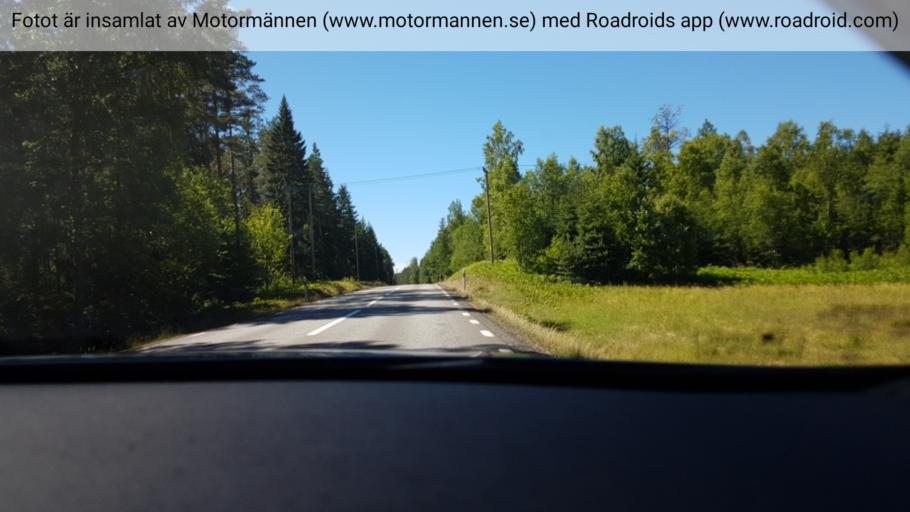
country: SE
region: Joenkoeping
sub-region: Mullsjo Kommun
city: Mullsjoe
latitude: 57.7942
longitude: 13.8409
